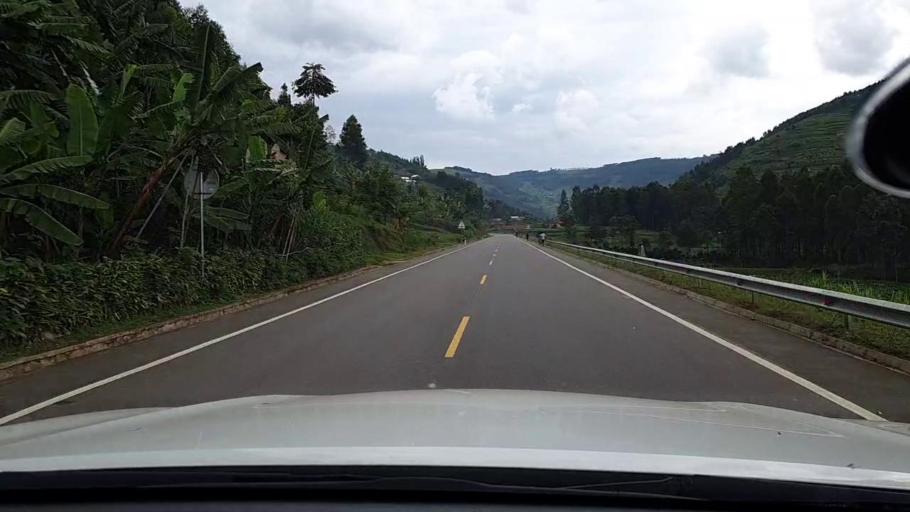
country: RW
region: Northern Province
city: Byumba
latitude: -1.6321
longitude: 29.9276
